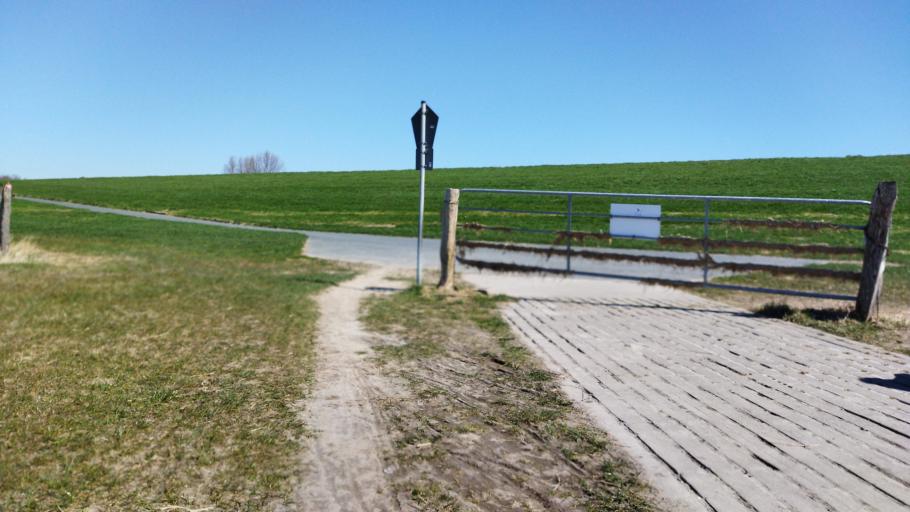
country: DE
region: Lower Saxony
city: Wremen
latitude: 53.6393
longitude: 8.4987
